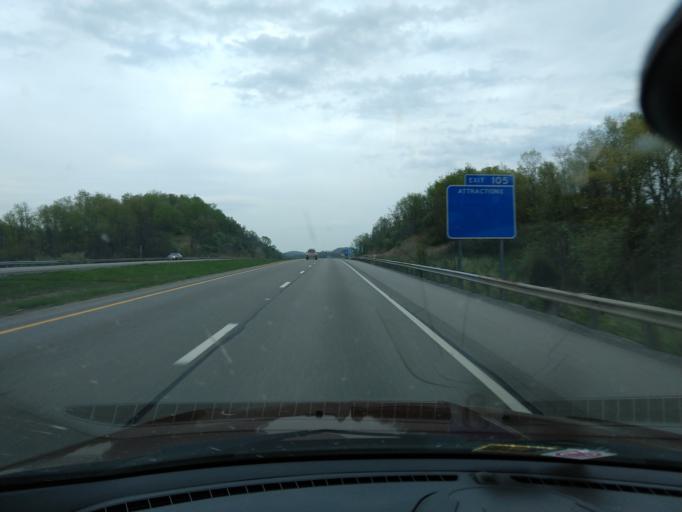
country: US
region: West Virginia
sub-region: Lewis County
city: Weston
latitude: 39.0820
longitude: -80.3998
